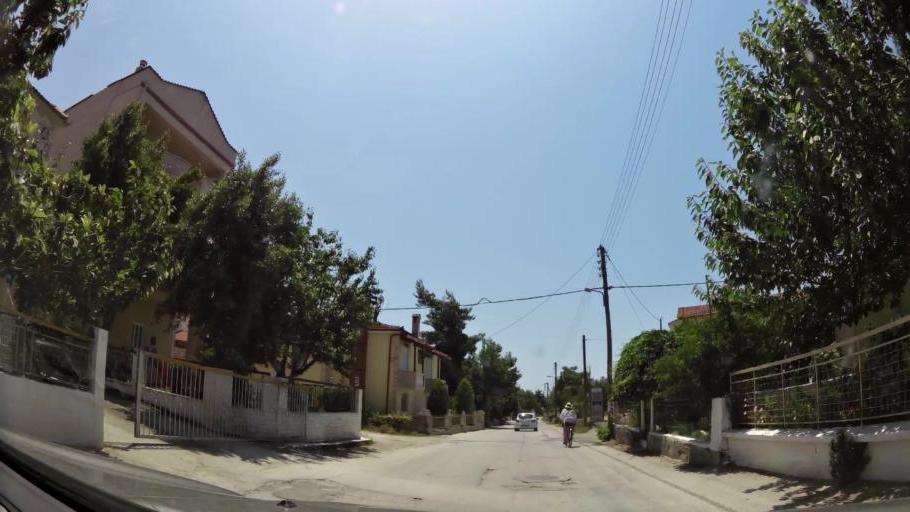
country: GR
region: Central Macedonia
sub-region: Nomos Thessalonikis
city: Epanomi
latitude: 40.4286
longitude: 22.9236
